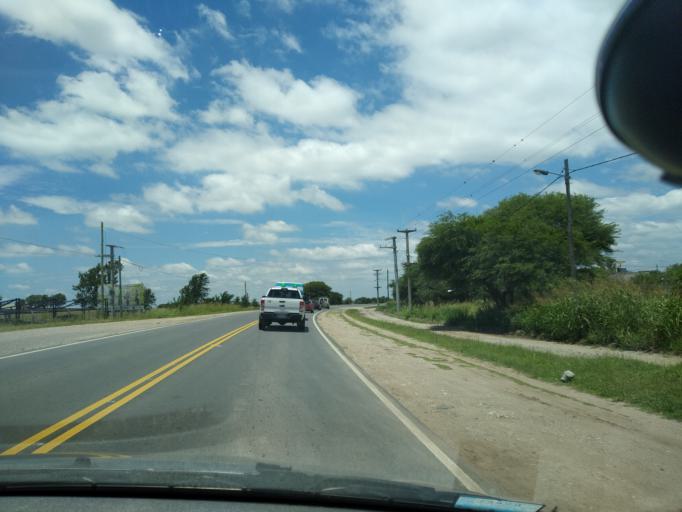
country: AR
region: Cordoba
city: Alta Gracia
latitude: -31.6253
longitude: -64.4356
